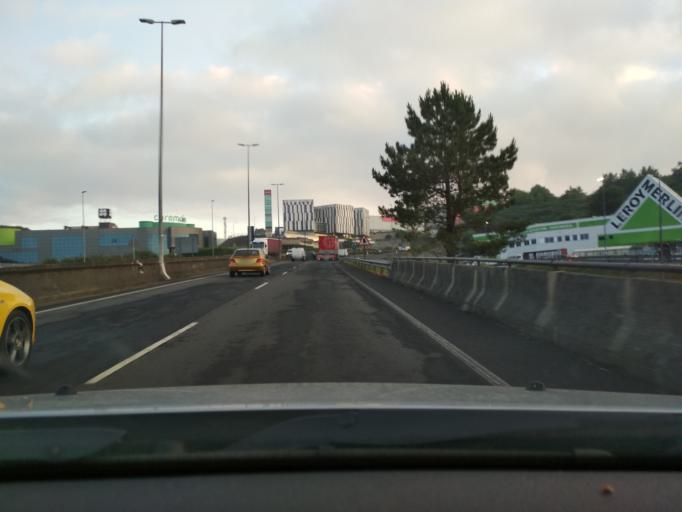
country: ES
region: Galicia
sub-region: Provincia da Coruna
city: Santiago de Compostela
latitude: 42.9023
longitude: -8.5114
